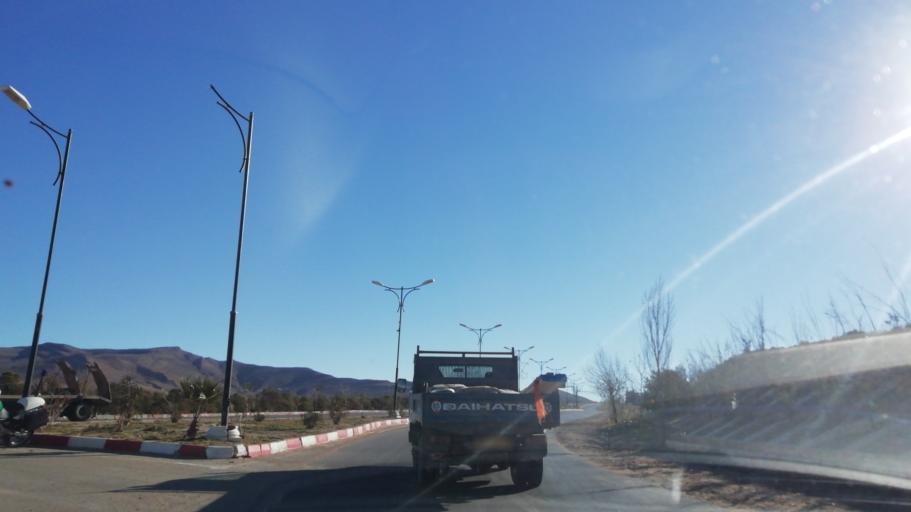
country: DZ
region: El Bayadh
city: El Bayadh
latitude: 33.6570
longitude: 1.0677
